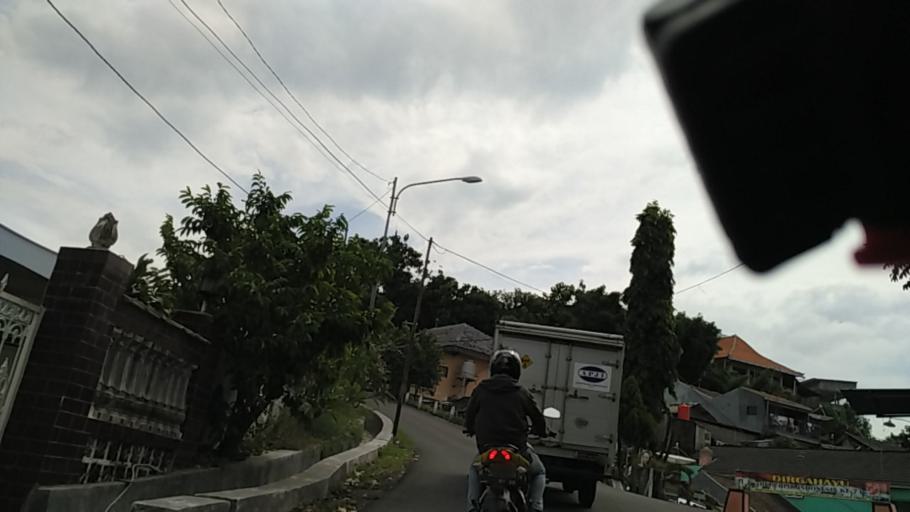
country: ID
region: Central Java
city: Semarang
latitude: -6.9975
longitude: 110.4113
